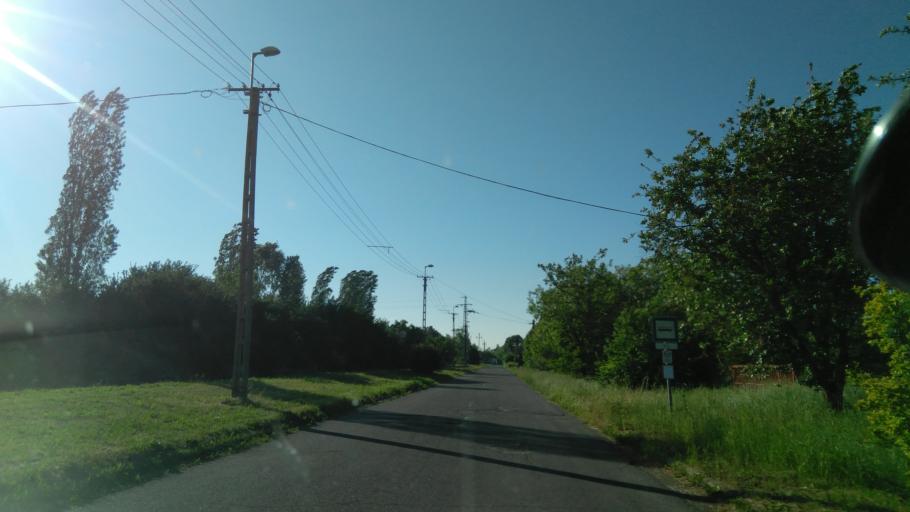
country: HU
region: Bekes
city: Gyula
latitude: 46.6382
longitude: 21.2557
